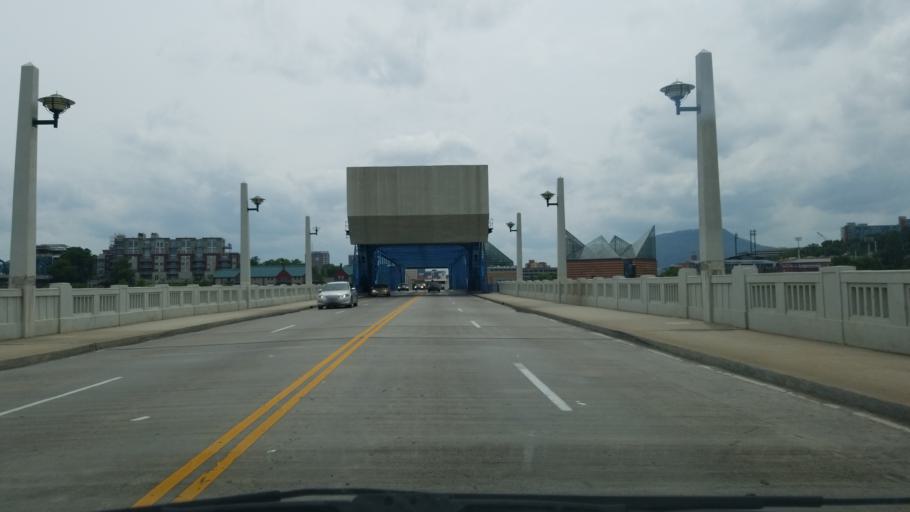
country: US
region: Tennessee
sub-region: Hamilton County
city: Chattanooga
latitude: 35.0597
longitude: -85.3090
